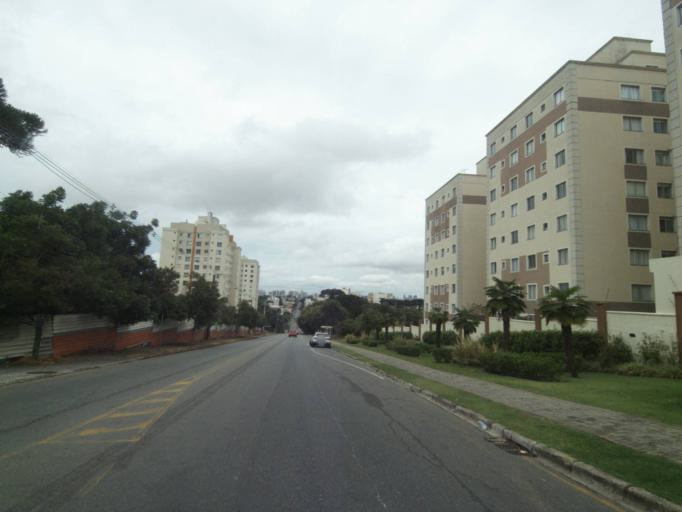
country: BR
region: Parana
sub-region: Curitiba
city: Curitiba
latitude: -25.4609
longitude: -49.3235
